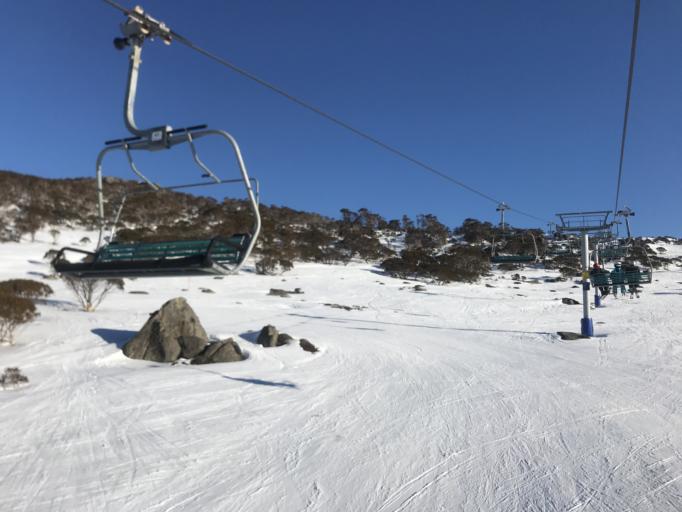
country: AU
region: New South Wales
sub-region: Snowy River
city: Jindabyne
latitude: -36.3904
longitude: 148.3960
